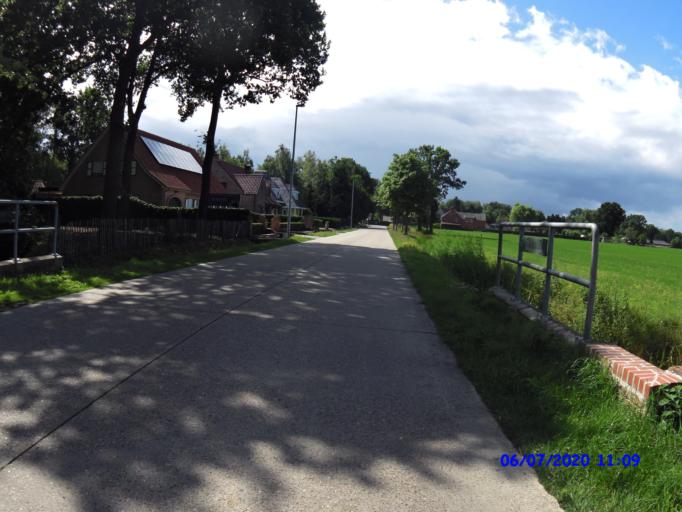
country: BE
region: Flanders
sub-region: Provincie Antwerpen
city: Oud-Turnhout
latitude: 51.3052
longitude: 5.0051
